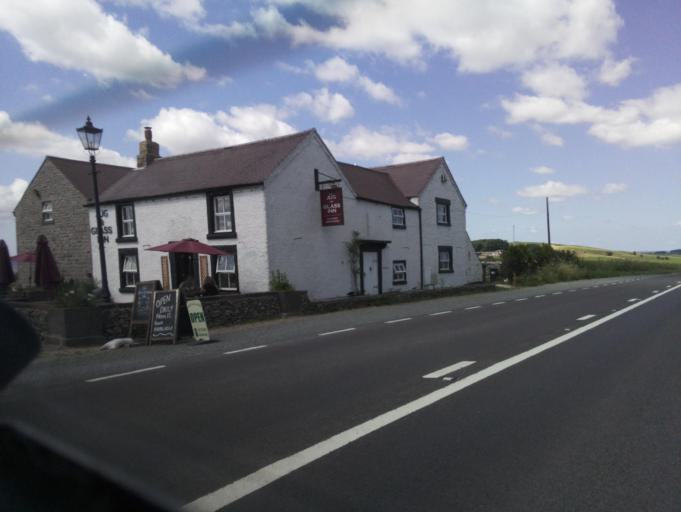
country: GB
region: England
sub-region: Derbyshire
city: Bakewell
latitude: 53.1501
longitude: -1.7668
